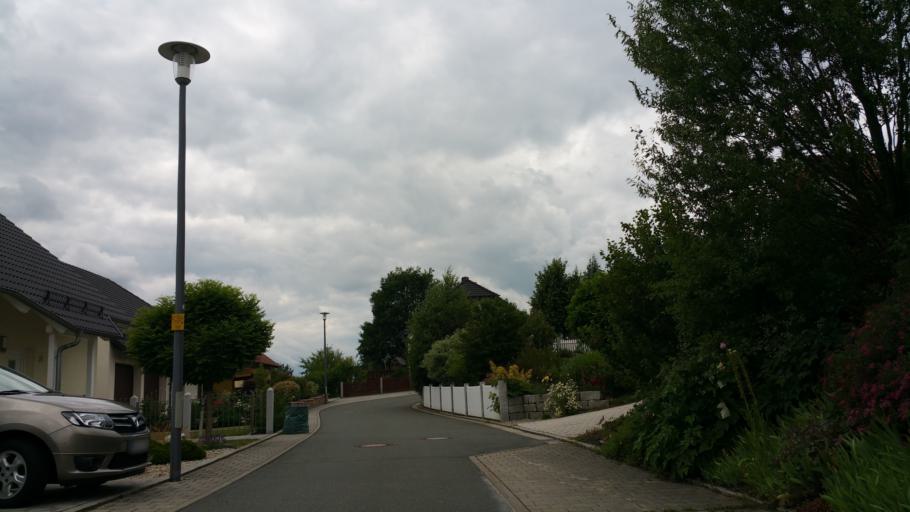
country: DE
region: Bavaria
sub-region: Upper Franconia
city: Oberkotzau
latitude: 50.2661
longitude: 11.9385
